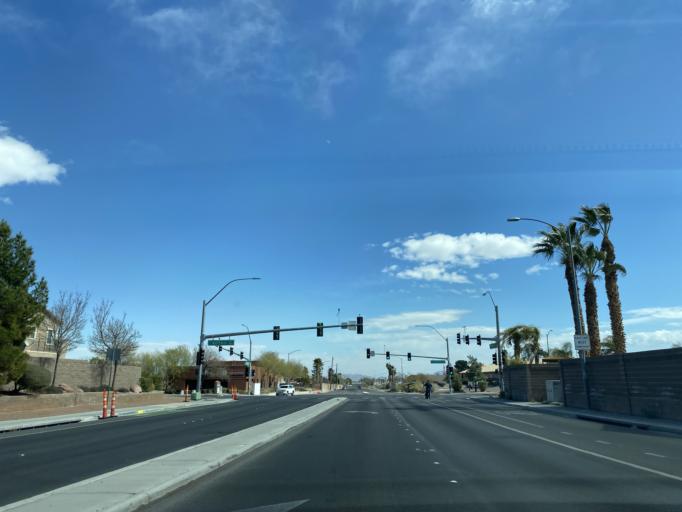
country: US
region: Nevada
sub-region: Clark County
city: Spring Valley
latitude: 36.2256
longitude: -115.2616
